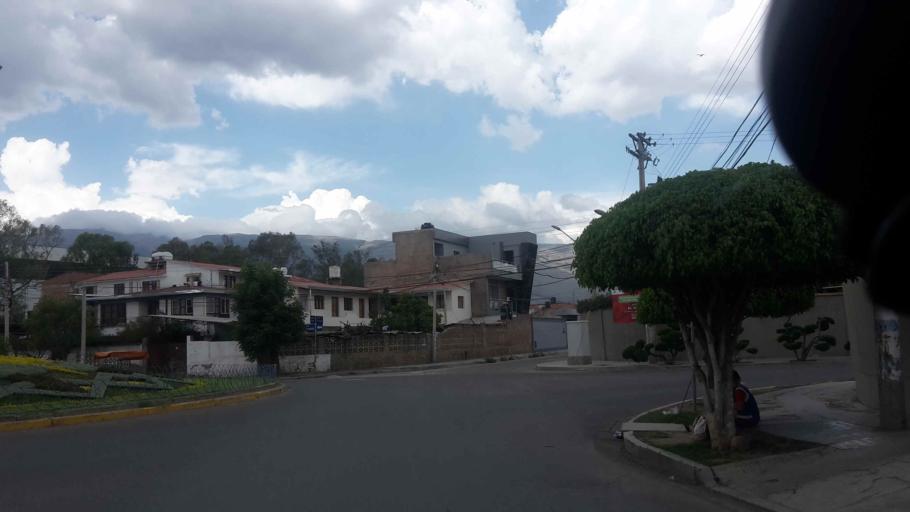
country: BO
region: Cochabamba
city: Cochabamba
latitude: -17.4032
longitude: -66.1741
